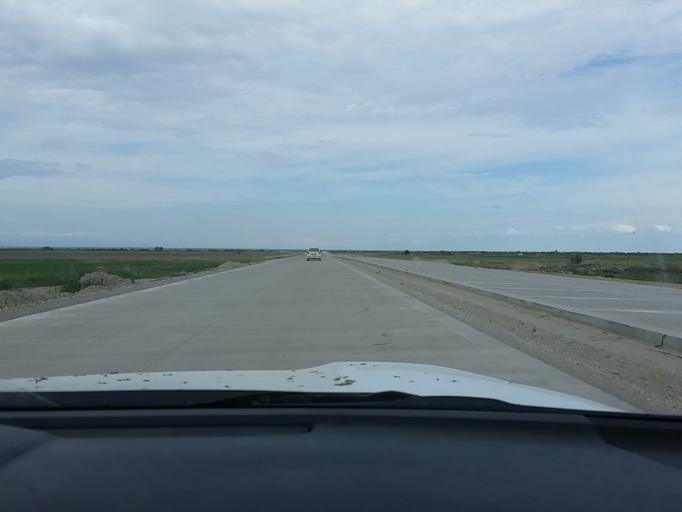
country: KZ
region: Almaty Oblysy
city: Zharkent
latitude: 44.0298
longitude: 79.9113
